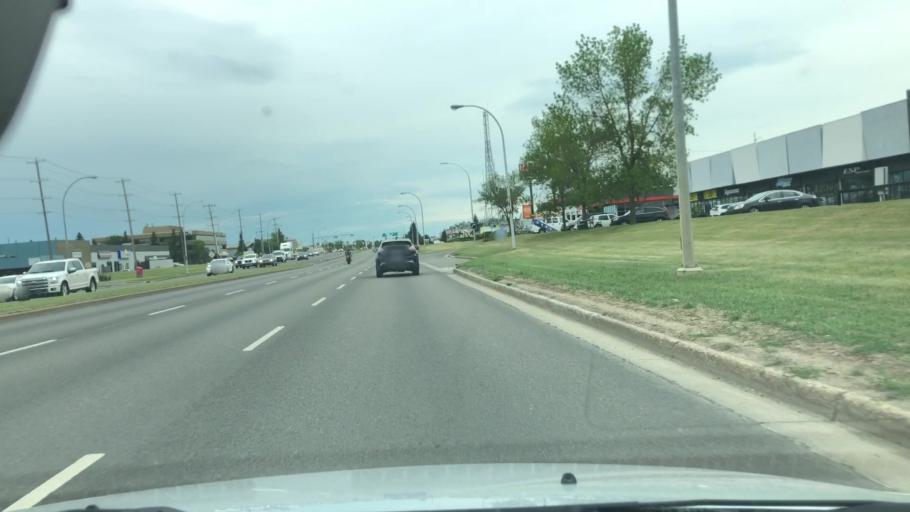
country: CA
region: Alberta
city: St. Albert
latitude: 53.5516
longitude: -113.6155
